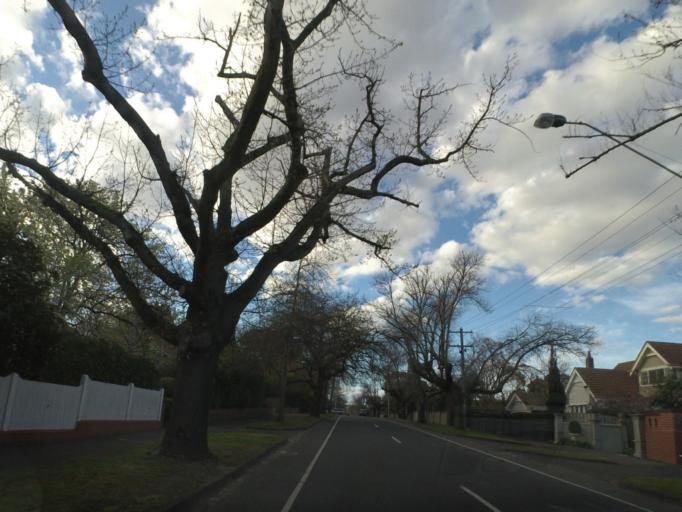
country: AU
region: Victoria
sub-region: Boroondara
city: Canterbury
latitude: -37.8205
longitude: 145.0798
